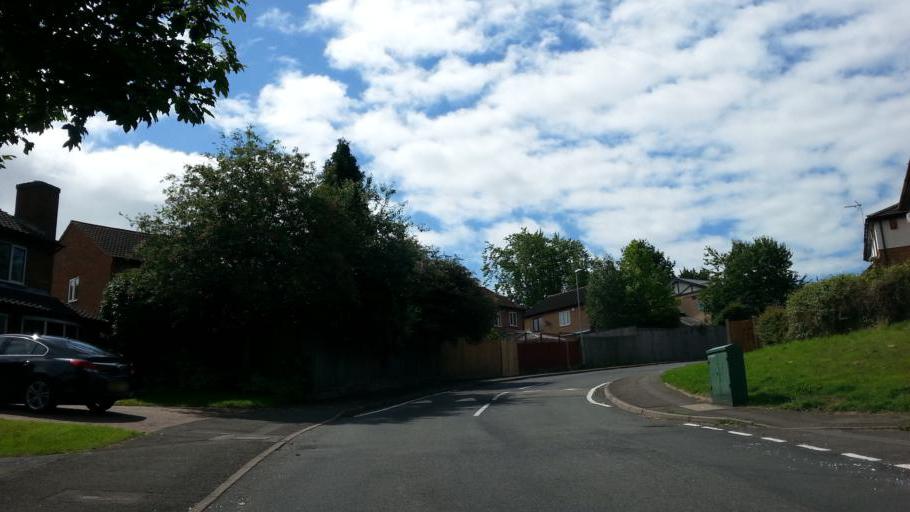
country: GB
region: England
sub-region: Northamptonshire
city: Earls Barton
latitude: 52.2691
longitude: -0.8079
